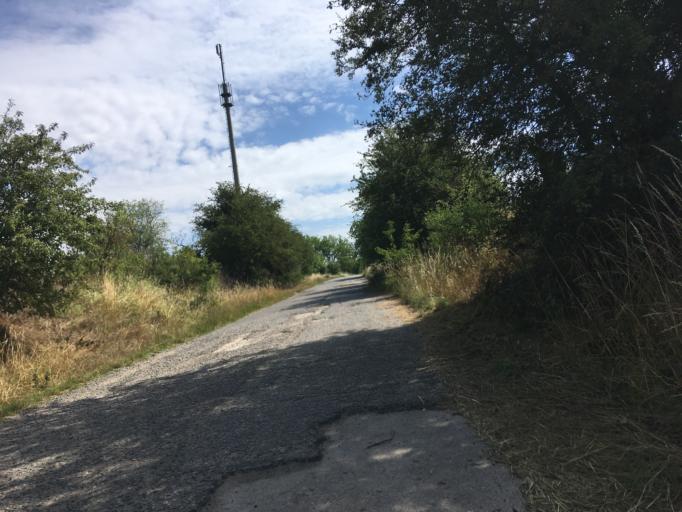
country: DE
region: Brandenburg
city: Casekow
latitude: 53.2034
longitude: 14.1442
